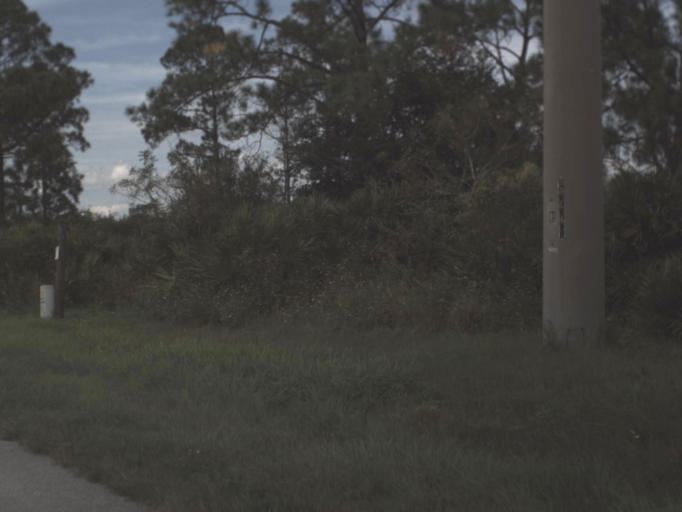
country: US
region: Florida
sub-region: Highlands County
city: Placid Lakes
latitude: 27.2086
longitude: -81.3691
